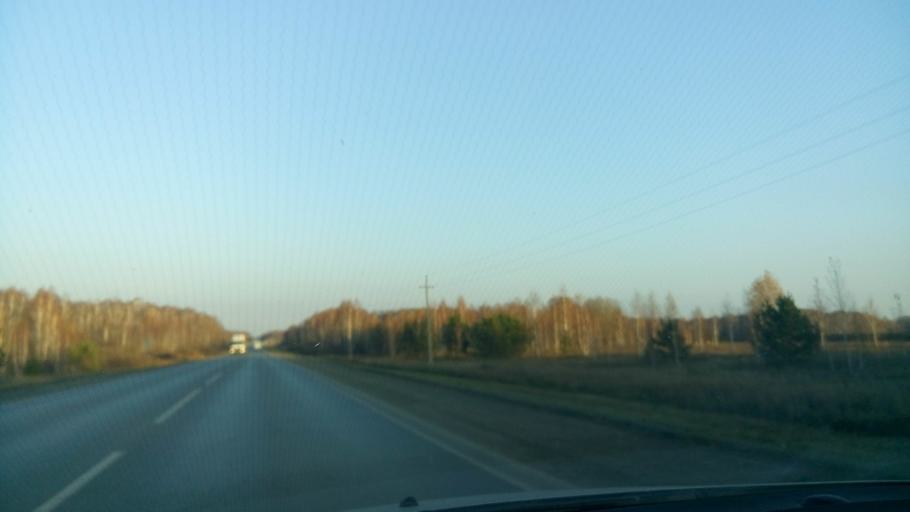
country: RU
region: Sverdlovsk
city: Bogdanovich
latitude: 56.7542
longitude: 62.1324
